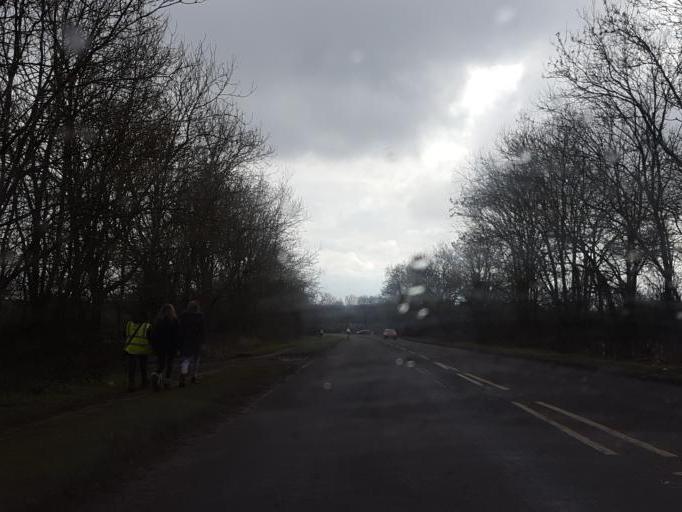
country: GB
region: England
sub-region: Buckinghamshire
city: Stokenchurch
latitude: 51.6665
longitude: -0.9225
